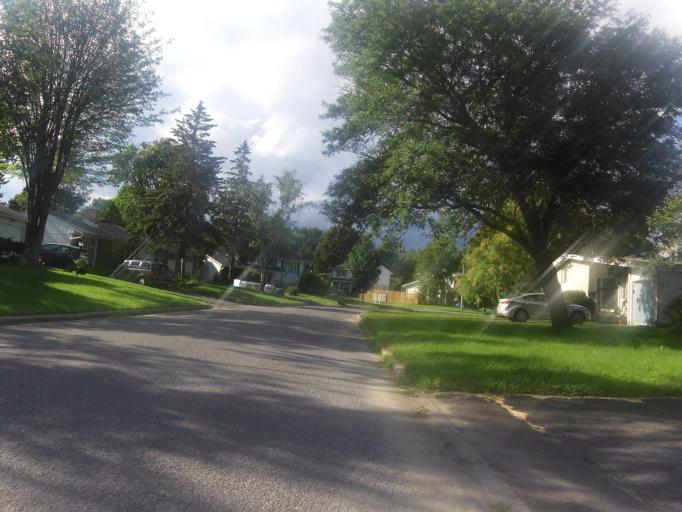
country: CA
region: Ontario
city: Bells Corners
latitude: 45.3300
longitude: -75.7876
